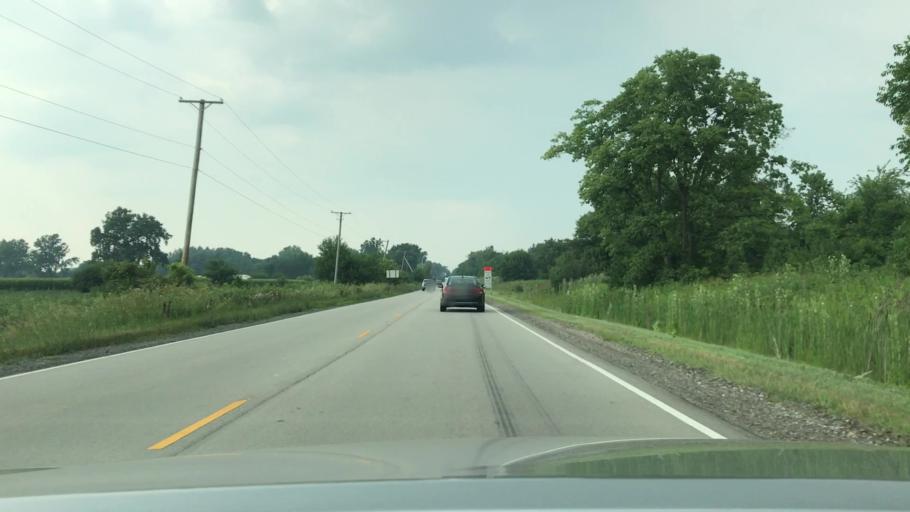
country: US
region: Illinois
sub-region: Will County
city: Plainfield
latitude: 41.6604
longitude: -88.2366
